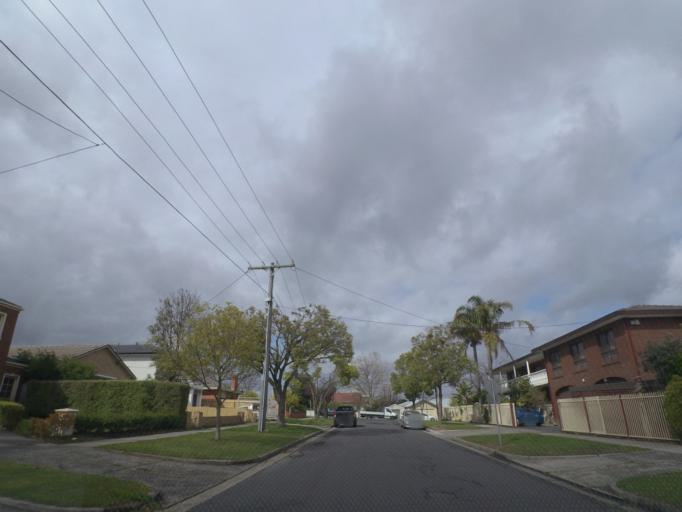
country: AU
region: Victoria
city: Mitcham
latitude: -37.8138
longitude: 145.1892
